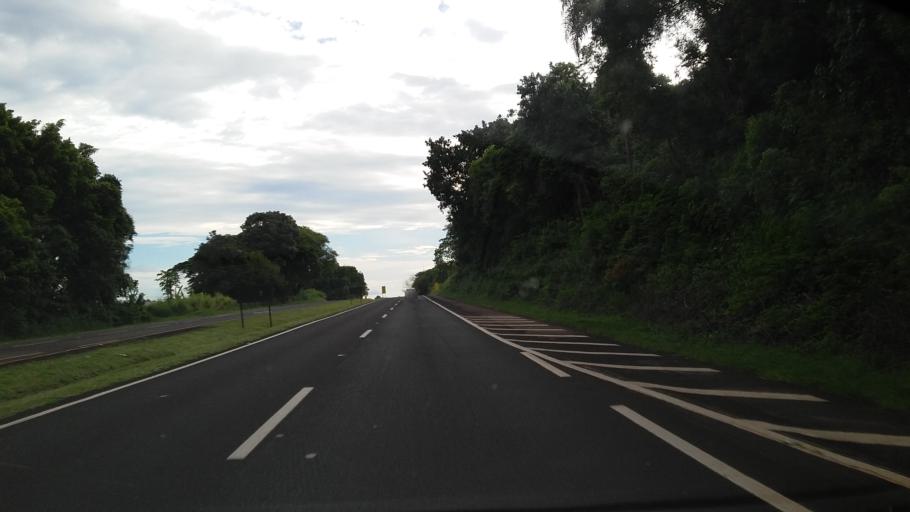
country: BR
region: Parana
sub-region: Paicandu
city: Paicandu
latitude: -23.5061
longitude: -52.0211
